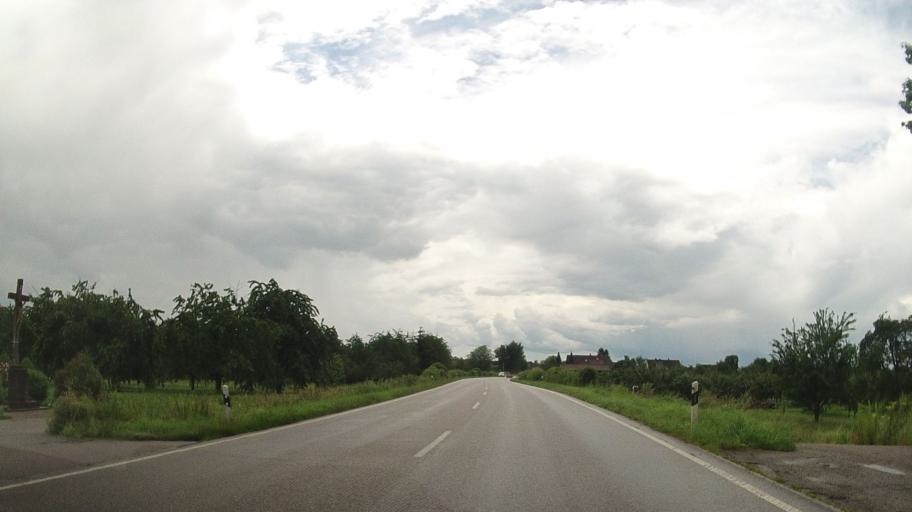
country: DE
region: Baden-Wuerttemberg
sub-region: Freiburg Region
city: Renchen
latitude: 48.6094
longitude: 8.0367
